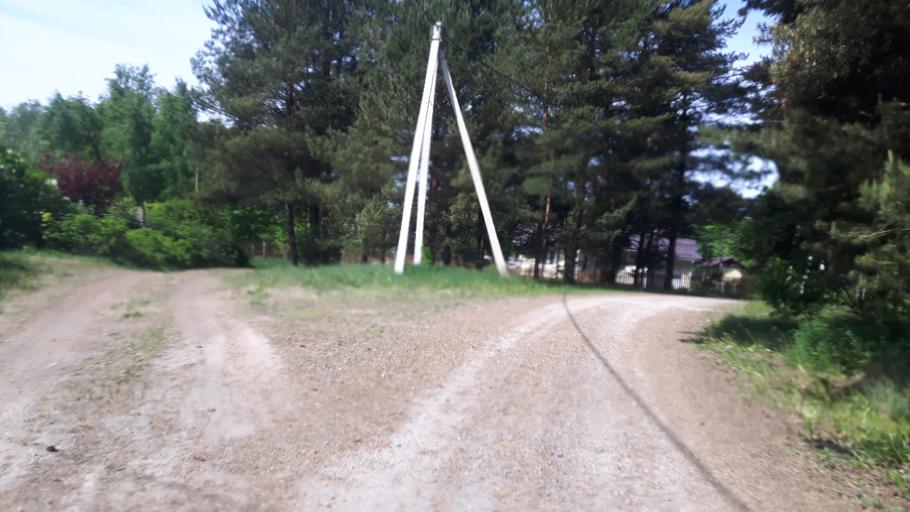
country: RU
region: Leningrad
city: Vistino
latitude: 59.6750
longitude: 28.4417
